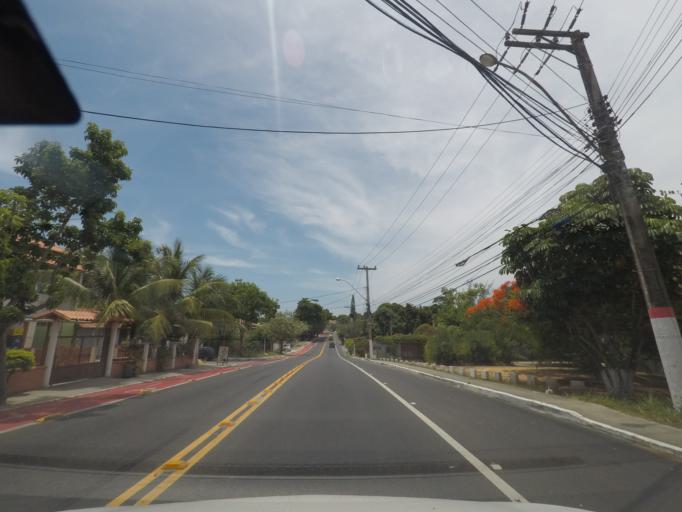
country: BR
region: Rio de Janeiro
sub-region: Marica
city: Marica
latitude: -22.9399
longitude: -42.8297
